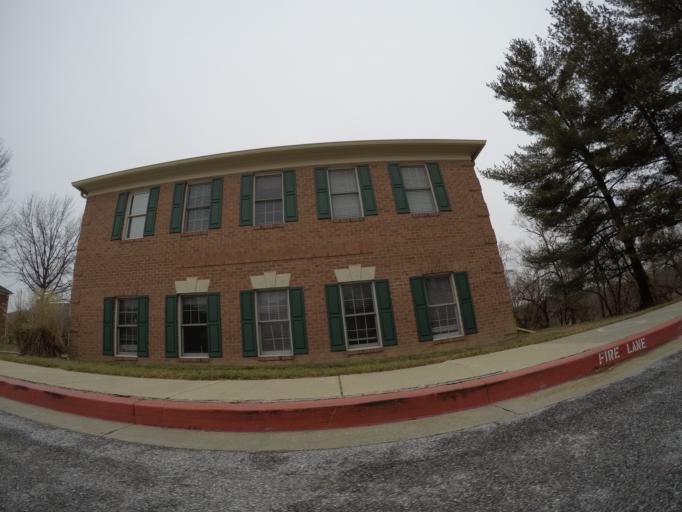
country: US
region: Maryland
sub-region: Howard County
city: Columbia
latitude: 39.2452
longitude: -76.8356
